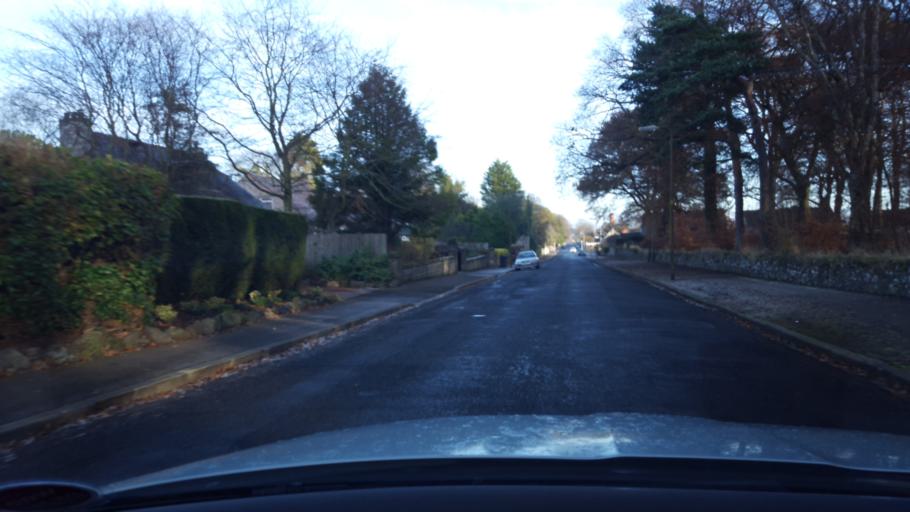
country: GB
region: Scotland
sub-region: Fife
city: Tayport
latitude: 56.4714
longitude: -2.8574
